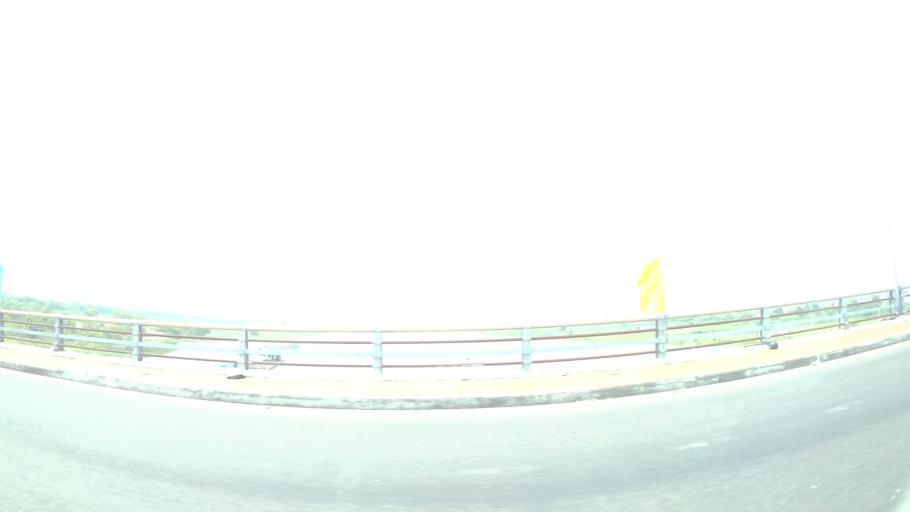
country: VN
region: Da Nang
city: Cam Le
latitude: 16.0081
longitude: 108.2073
